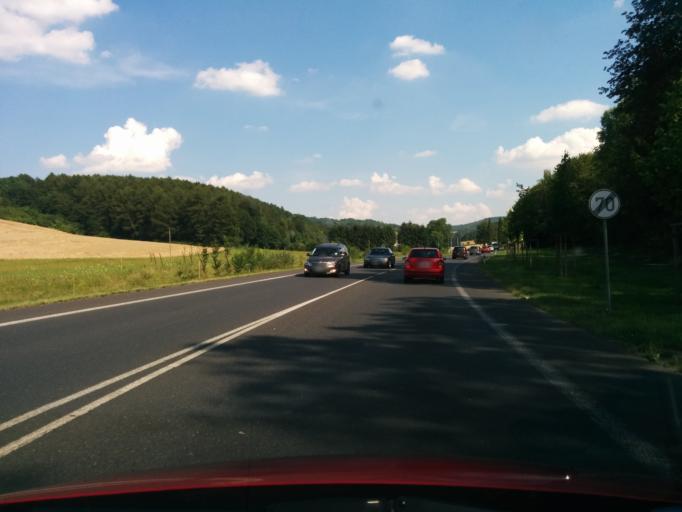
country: DE
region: Lower Saxony
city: Goettingen
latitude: 51.5532
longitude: 9.9662
